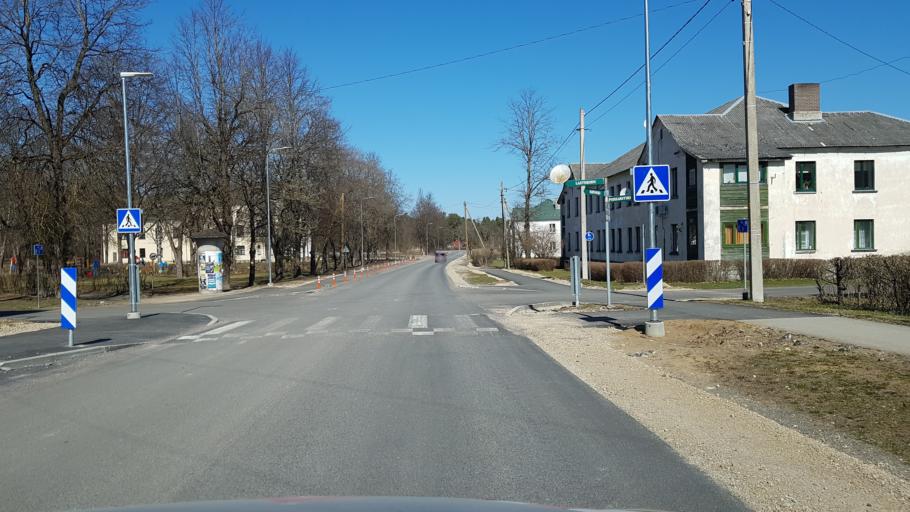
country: EE
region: Ida-Virumaa
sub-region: Kohtla-Nomme vald
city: Kohtla-Nomme
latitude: 59.3550
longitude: 27.1917
